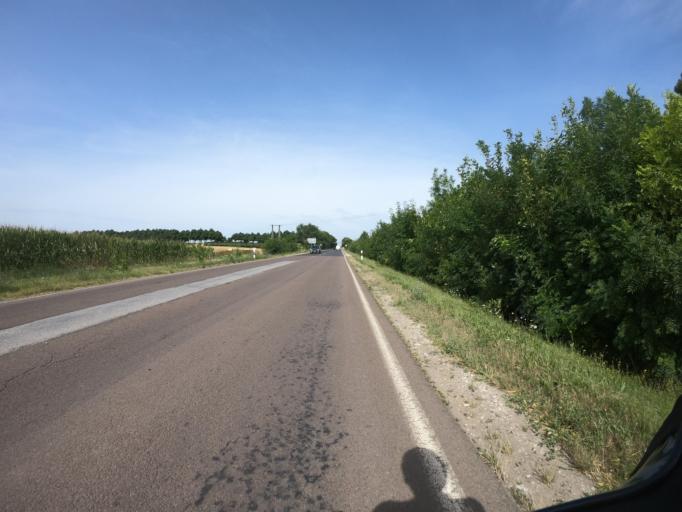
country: HU
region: Jasz-Nagykun-Szolnok
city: Tiszafured
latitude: 47.6042
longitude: 20.7828
